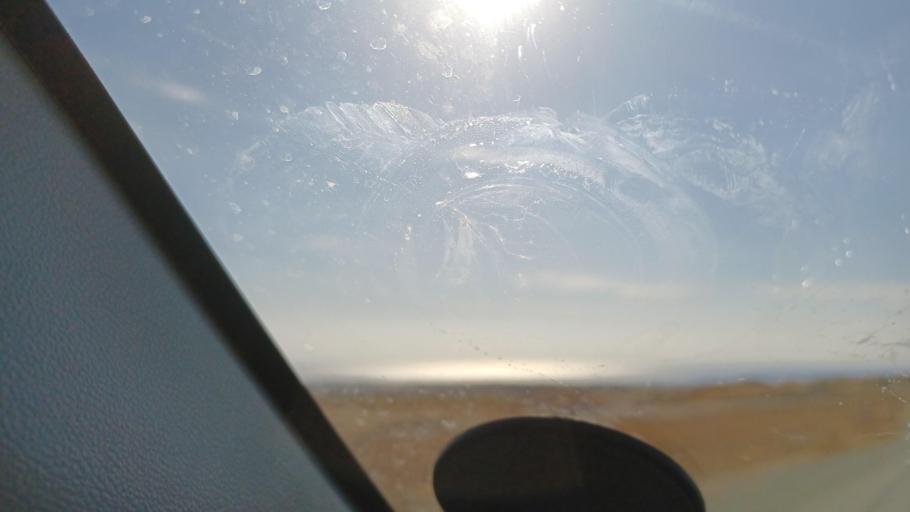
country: CY
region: Pafos
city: Mesogi
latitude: 34.7357
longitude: 32.5517
